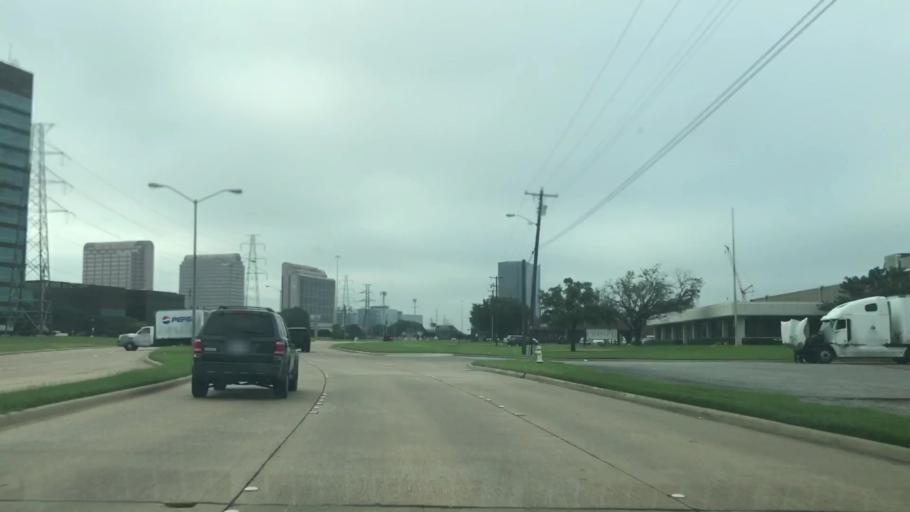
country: US
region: Texas
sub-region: Dallas County
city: Addison
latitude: 32.9372
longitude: -96.8247
